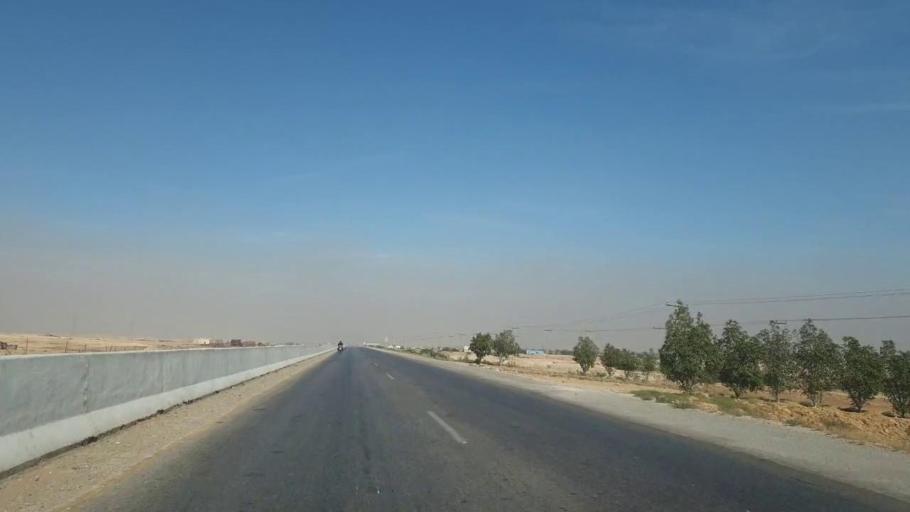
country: PK
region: Sindh
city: Jamshoro
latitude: 25.5030
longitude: 68.2729
